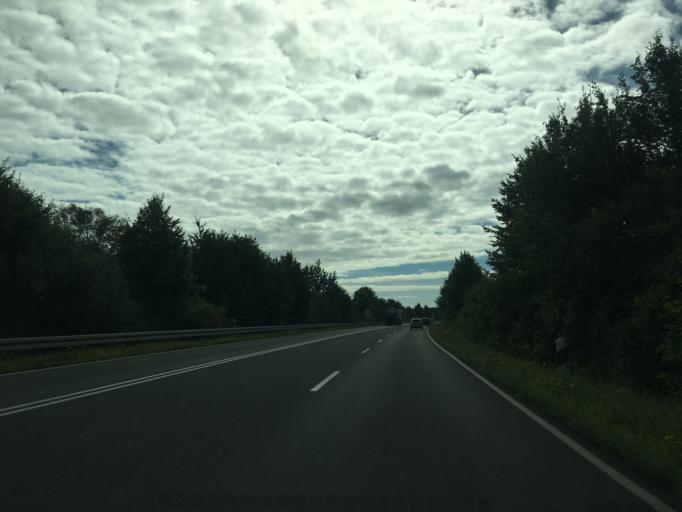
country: DE
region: Lower Saxony
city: Hessisch Oldendorf
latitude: 52.1713
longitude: 9.2292
